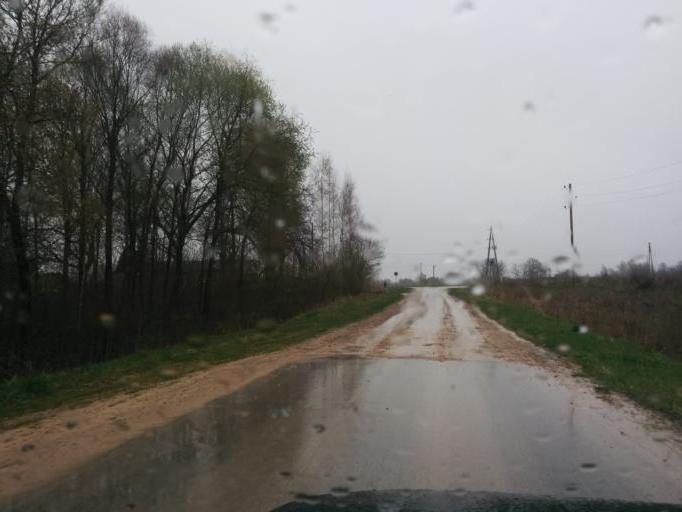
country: LV
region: Lecava
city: Iecava
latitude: 56.6234
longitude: 24.1839
